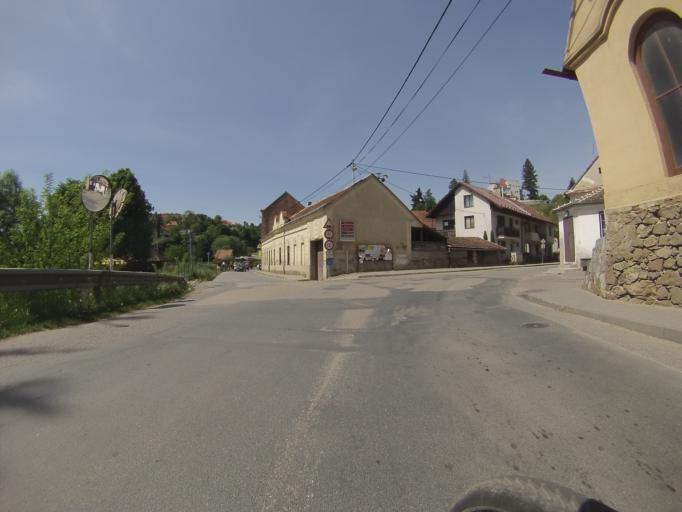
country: CZ
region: South Moravian
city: Bilovice nad Svitavou
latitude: 49.2478
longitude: 16.6740
